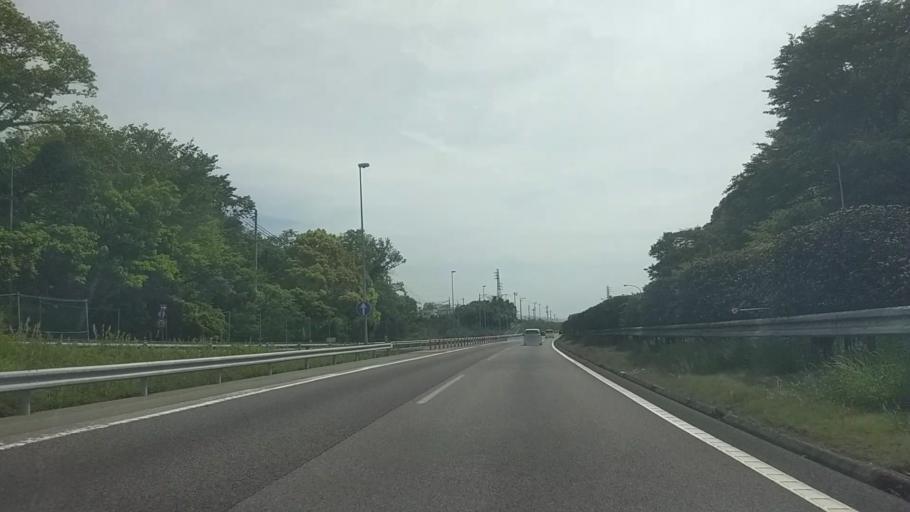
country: JP
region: Aichi
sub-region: Tokai-shi
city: Toyokawa
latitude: 34.8505
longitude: 137.3624
